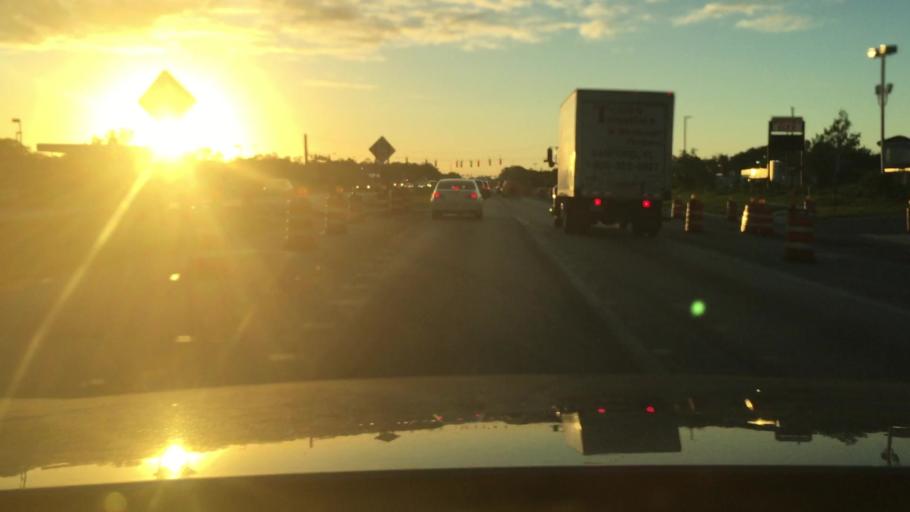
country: US
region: Florida
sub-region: Osceola County
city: Saint Cloud
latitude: 28.2557
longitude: -81.3202
